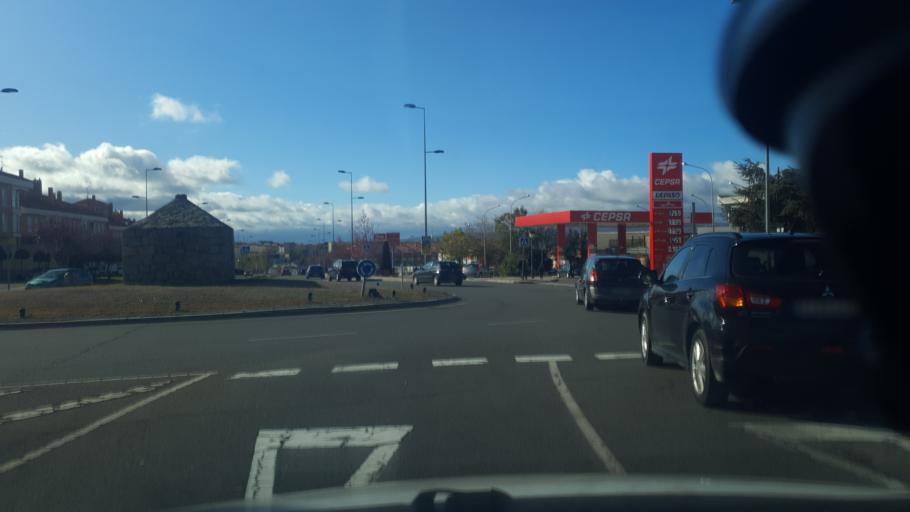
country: ES
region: Castille and Leon
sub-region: Provincia de Avila
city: Avila
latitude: 40.6621
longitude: -4.6734
